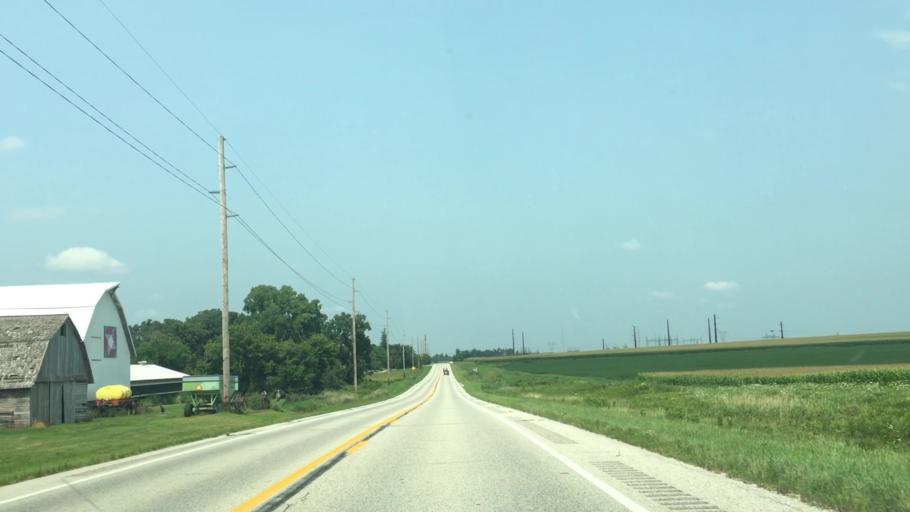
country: US
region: Iowa
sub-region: Fayette County
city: Oelwein
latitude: 42.5744
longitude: -91.9047
